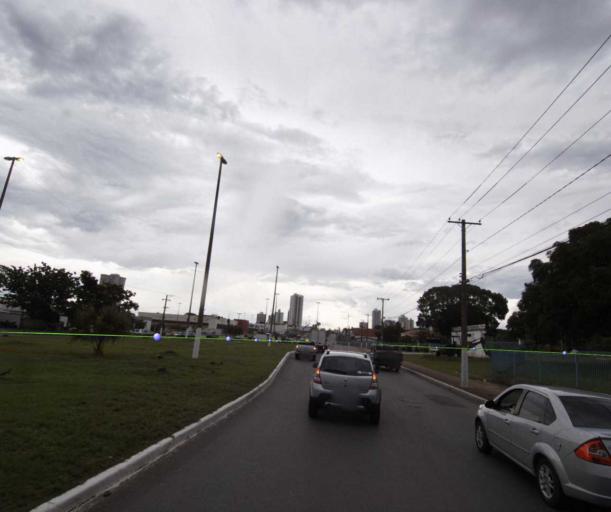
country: BR
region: Mato Grosso
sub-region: Cuiaba
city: Cuiaba
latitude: -15.6198
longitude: -56.0667
